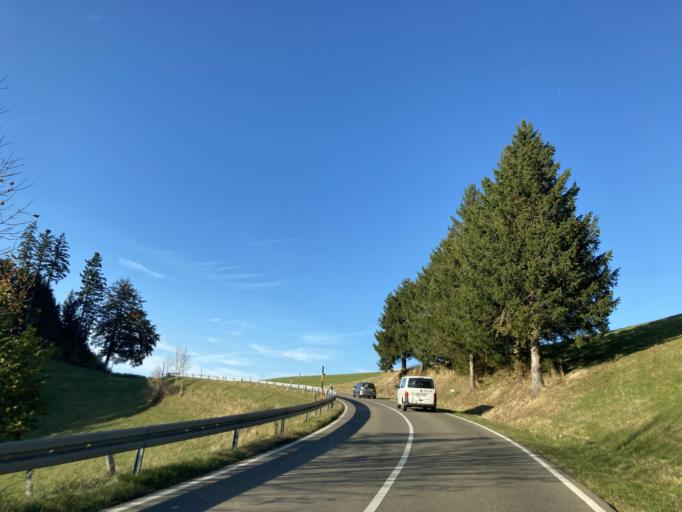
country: DE
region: Baden-Wuerttemberg
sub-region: Freiburg Region
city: Sankt Margen
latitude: 47.9771
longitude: 8.0962
